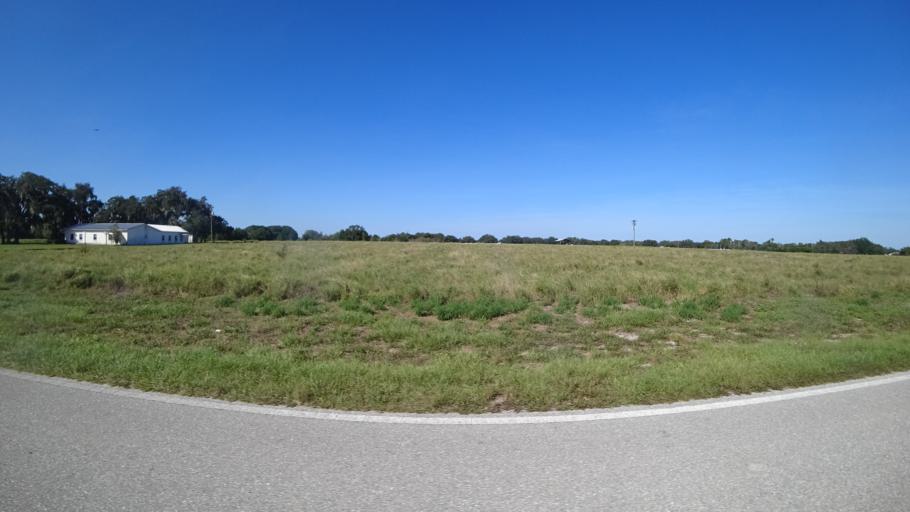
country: US
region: Florida
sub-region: Hillsborough County
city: Wimauma
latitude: 27.5921
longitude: -82.1987
